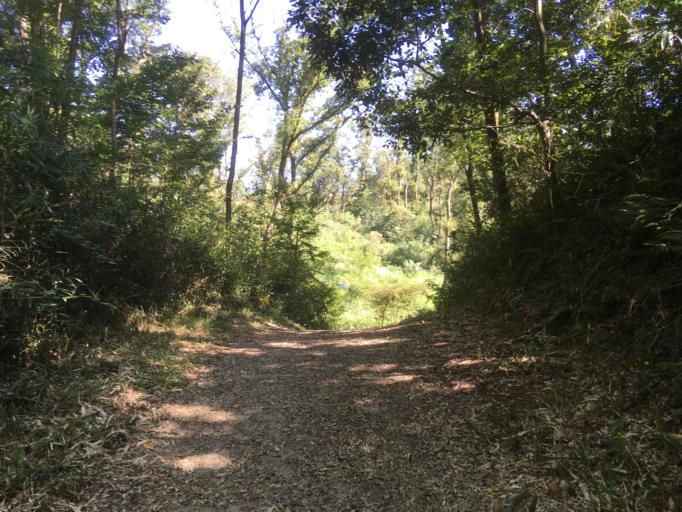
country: JP
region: Osaka
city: Daitocho
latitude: 34.7286
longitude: 135.6682
